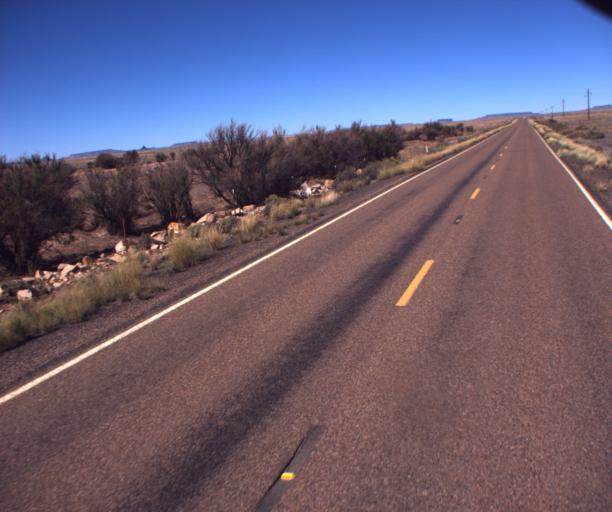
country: US
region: Arizona
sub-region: Navajo County
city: Holbrook
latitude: 35.0809
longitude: -110.0987
